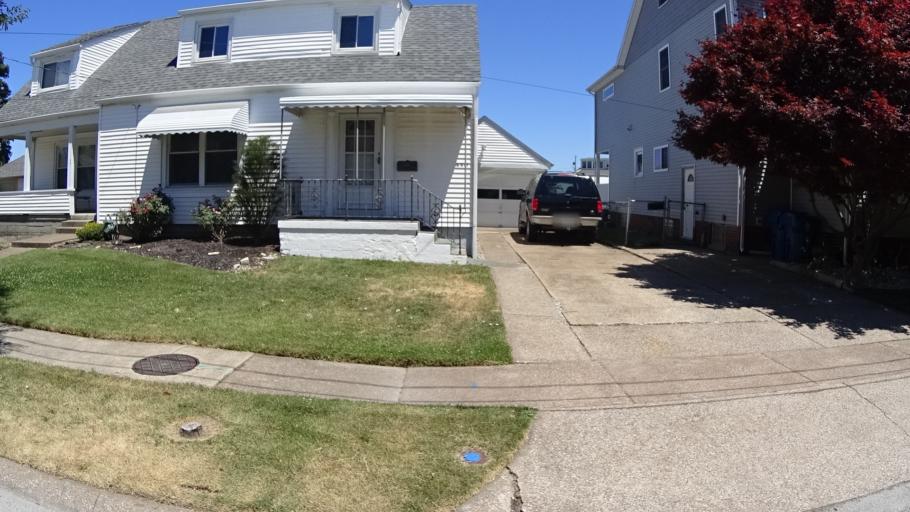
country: US
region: Ohio
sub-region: Erie County
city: Sandusky
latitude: 41.4558
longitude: -82.6978
